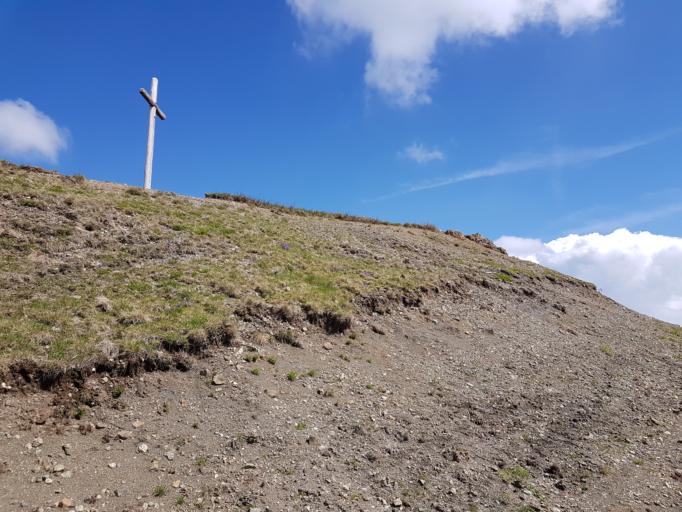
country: IT
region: Liguria
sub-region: Provincia di Genova
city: Santo Stefano d'Aveto
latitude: 44.5553
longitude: 9.4926
